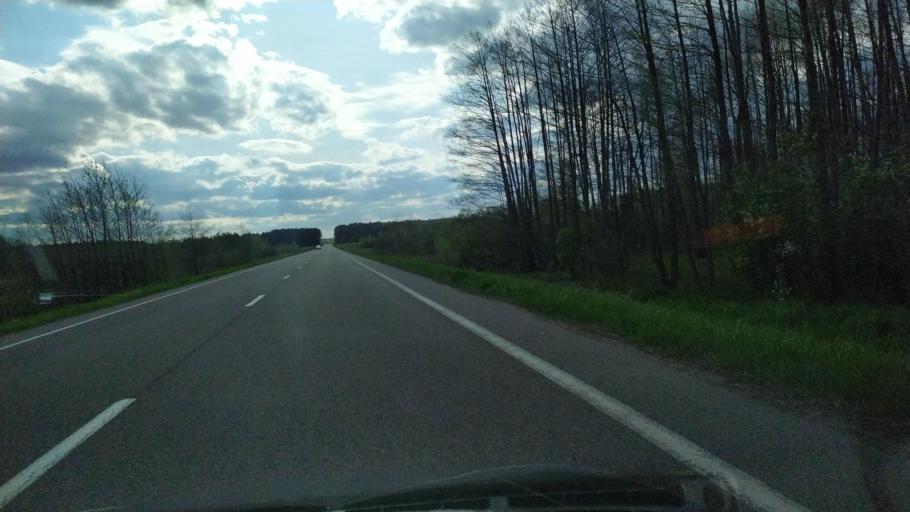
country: BY
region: Brest
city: Pruzhany
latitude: 52.6970
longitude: 24.2476
